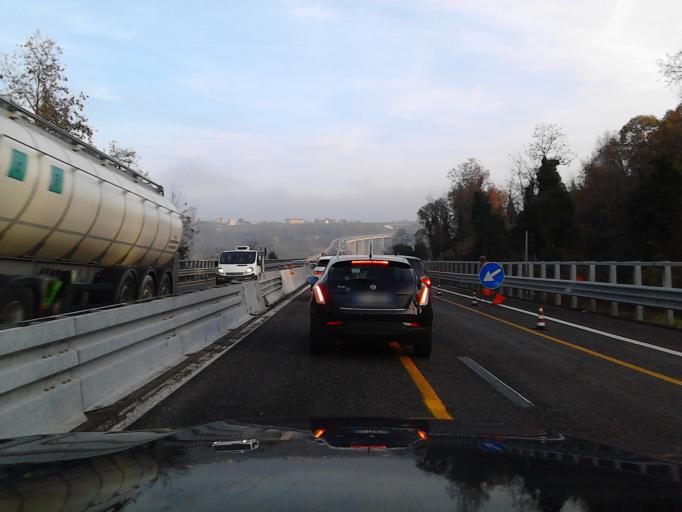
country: IT
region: Abruzzo
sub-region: Provincia di Chieti
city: Ortona
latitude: 42.3146
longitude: 14.4075
